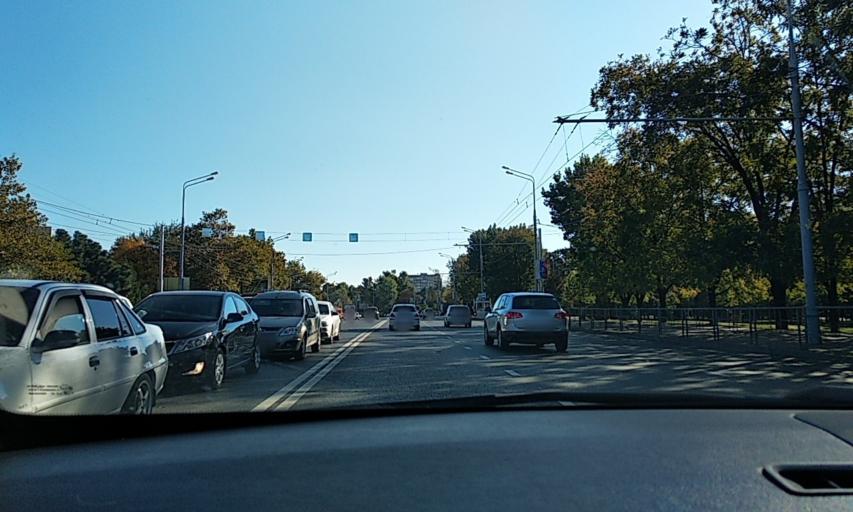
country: RU
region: Krasnodarskiy
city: Pashkovskiy
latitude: 45.0125
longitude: 39.0727
